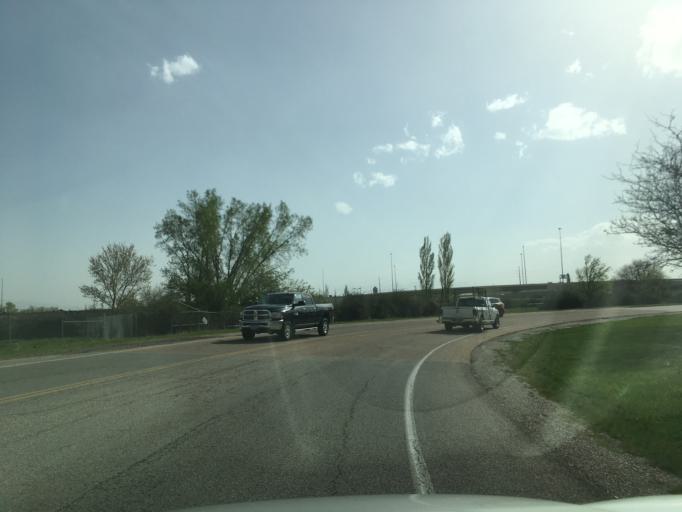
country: US
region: Utah
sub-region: Davis County
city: Farmington
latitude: 40.9905
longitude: -111.8969
